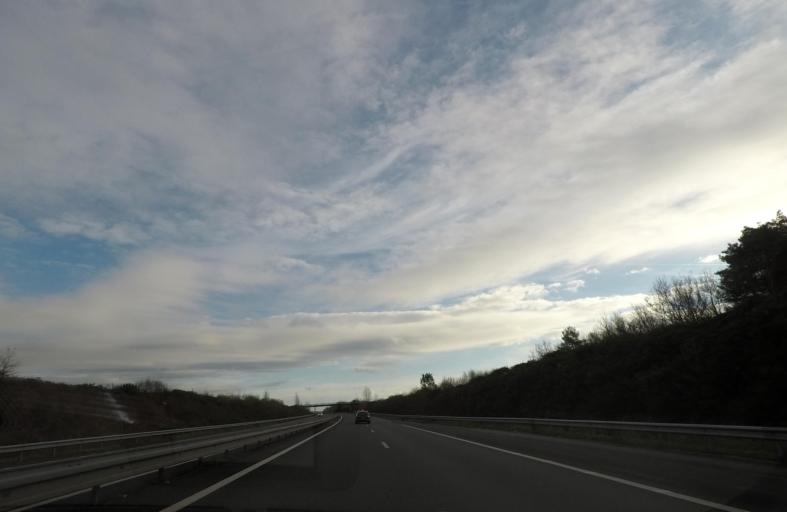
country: FR
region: Centre
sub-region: Departement du Loir-et-Cher
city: Villefranche-sur-Cher
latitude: 47.3201
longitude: 1.7740
